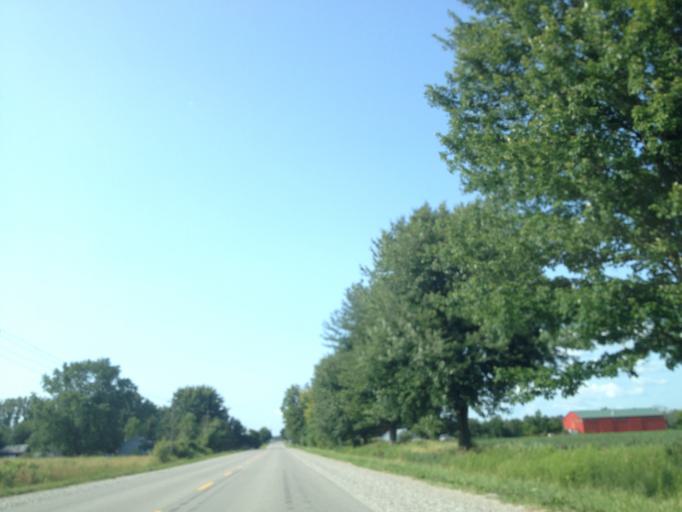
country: CA
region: Ontario
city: Aylmer
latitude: 42.8126
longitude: -80.8323
